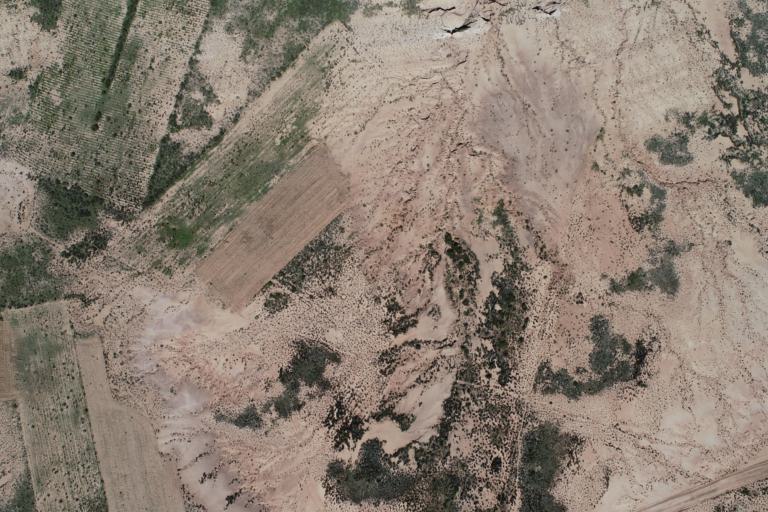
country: BO
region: La Paz
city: Patacamaya
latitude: -17.2936
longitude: -68.4951
